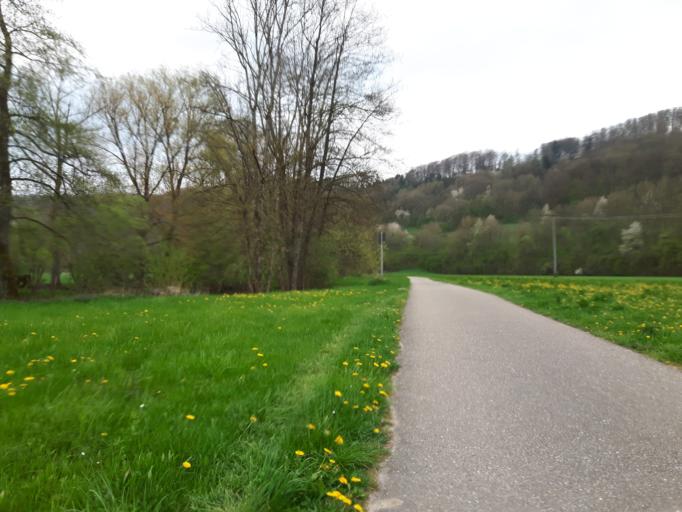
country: DE
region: Baden-Wuerttemberg
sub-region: Regierungsbezirk Stuttgart
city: Weissbach
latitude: 49.2906
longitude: 9.5993
